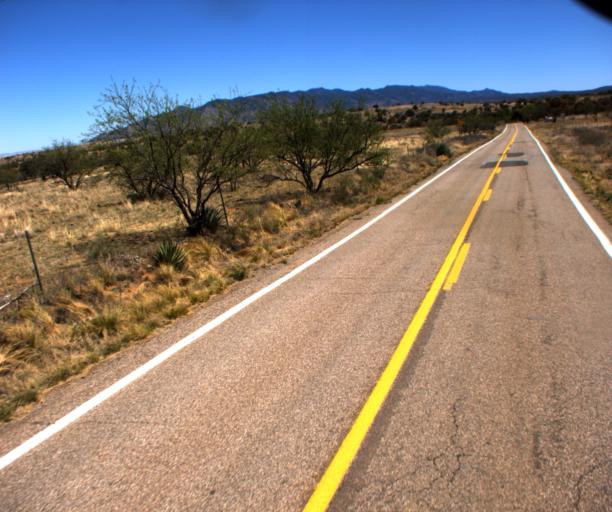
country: US
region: Arizona
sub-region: Cochise County
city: Huachuca City
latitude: 31.5809
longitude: -110.5578
